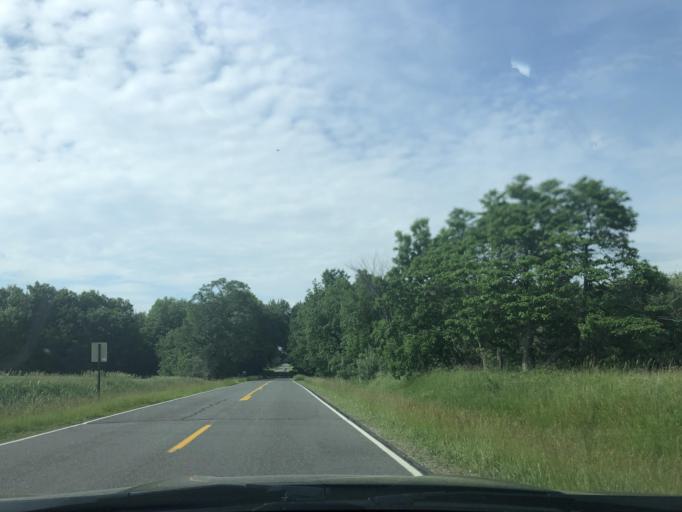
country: US
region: Michigan
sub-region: Clinton County
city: Bath
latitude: 42.8451
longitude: -84.4839
